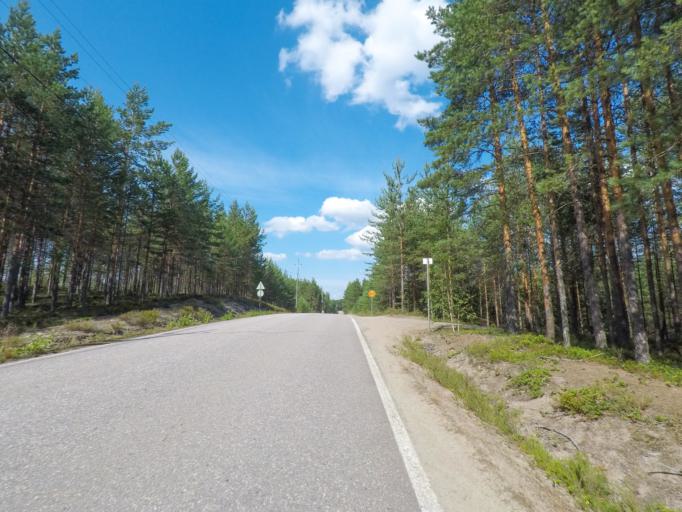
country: FI
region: Southern Savonia
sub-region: Mikkeli
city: Puumala
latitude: 61.4546
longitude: 28.1737
